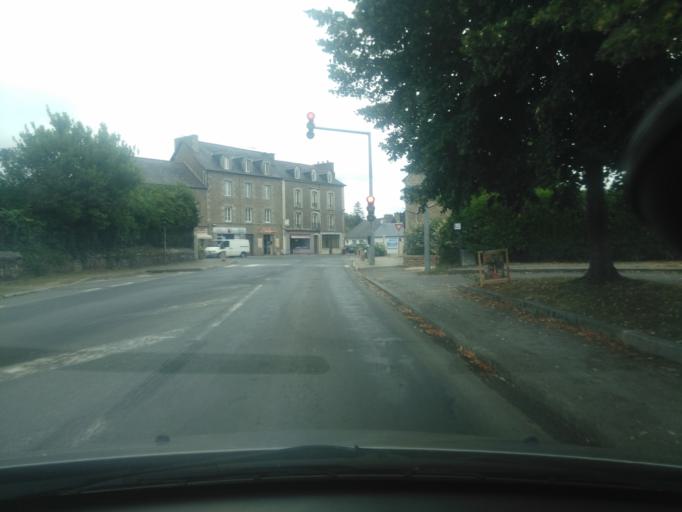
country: FR
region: Brittany
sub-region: Departement des Cotes-d'Armor
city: Lanvallay
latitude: 48.4542
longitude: -2.0264
